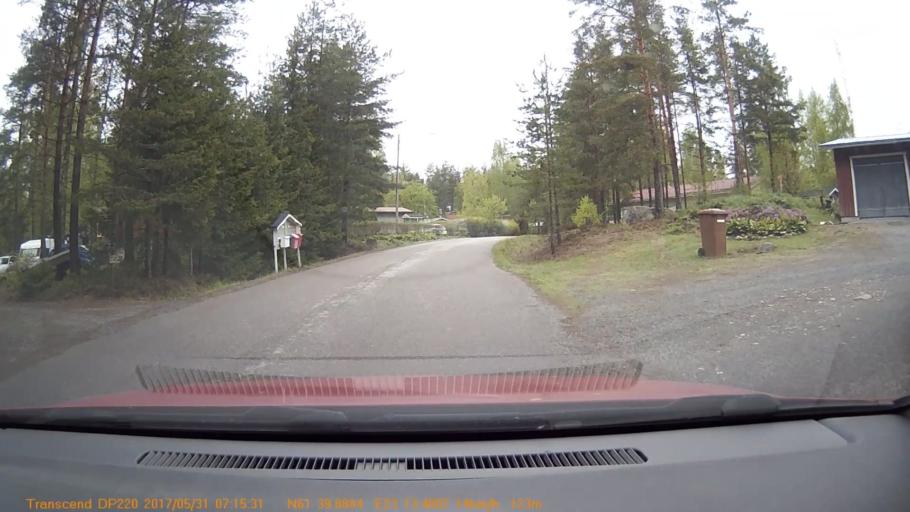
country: FI
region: Pirkanmaa
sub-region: Tampere
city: Haemeenkyroe
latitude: 61.6648
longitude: 23.2233
